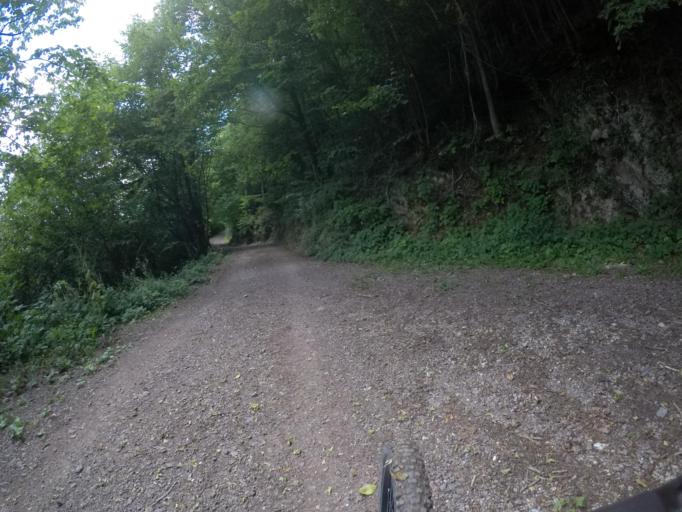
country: IT
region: Friuli Venezia Giulia
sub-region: Provincia di Udine
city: Arta Terme
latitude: 46.4813
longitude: 13.0626
